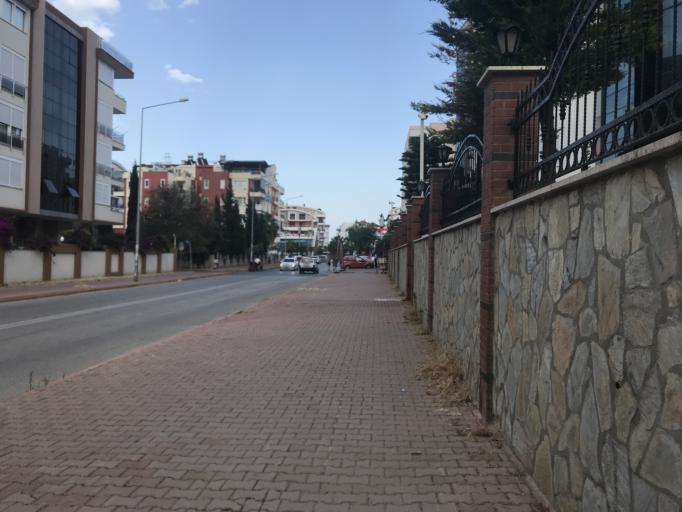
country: TR
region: Antalya
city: Cakirlar
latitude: 36.8495
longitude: 30.6118
